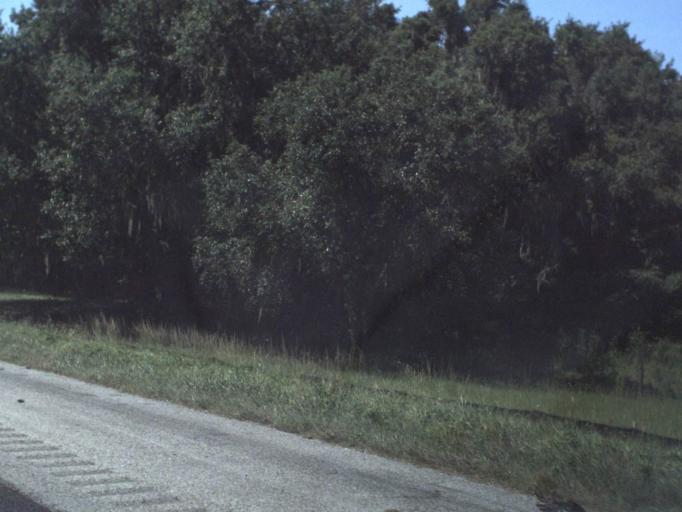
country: US
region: Florida
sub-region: Alachua County
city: Gainesville
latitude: 29.5559
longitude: -82.3432
